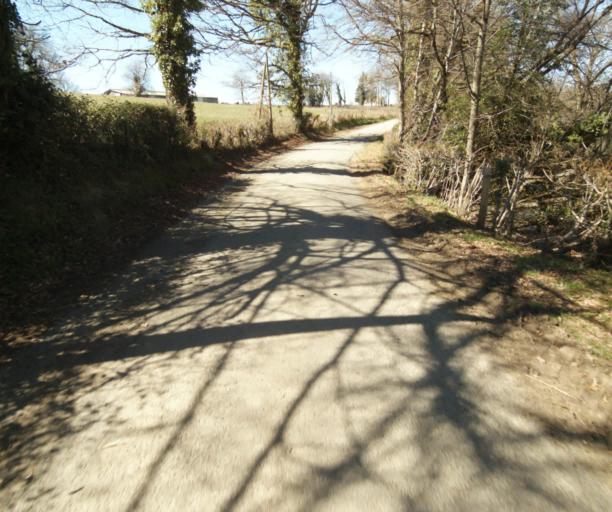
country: FR
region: Limousin
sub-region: Departement de la Correze
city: Saint-Clement
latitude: 45.3976
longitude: 1.6396
